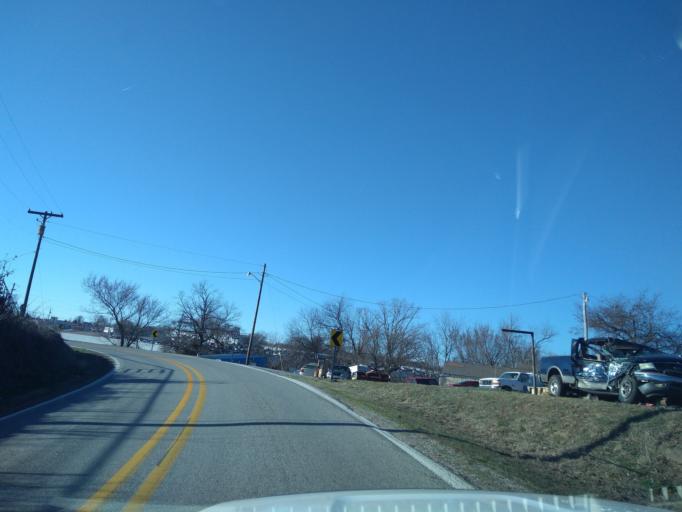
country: US
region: Arkansas
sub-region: Washington County
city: Lincoln
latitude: 35.9503
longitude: -94.3770
